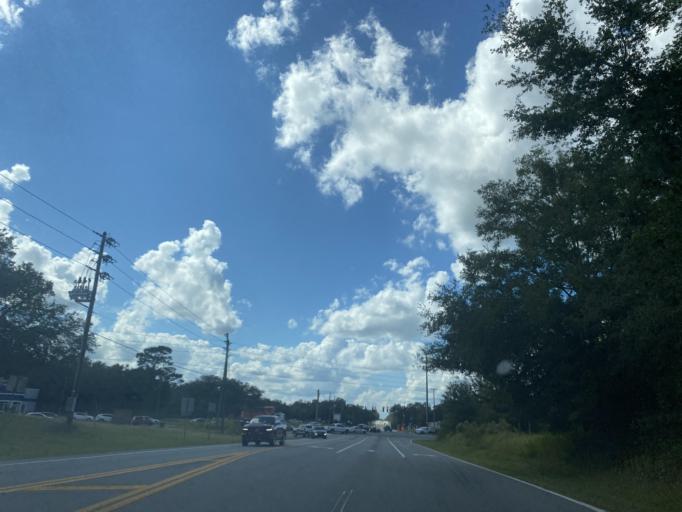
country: US
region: Florida
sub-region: Sumter County
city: The Villages
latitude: 28.9820
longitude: -81.9860
